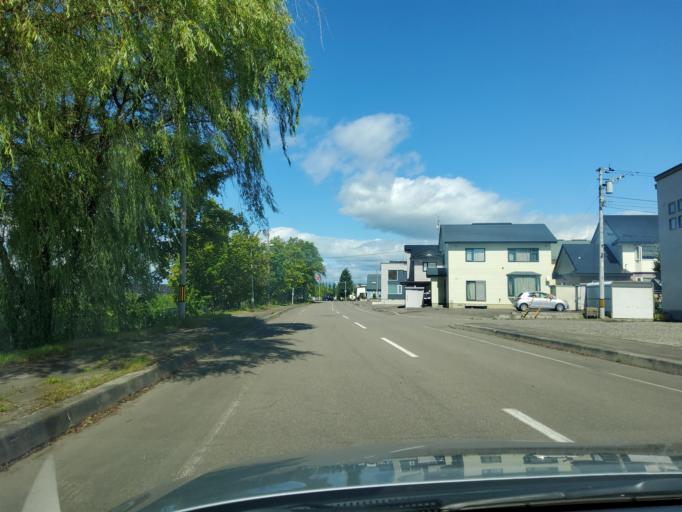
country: JP
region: Hokkaido
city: Otofuke
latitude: 42.9603
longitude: 143.1938
